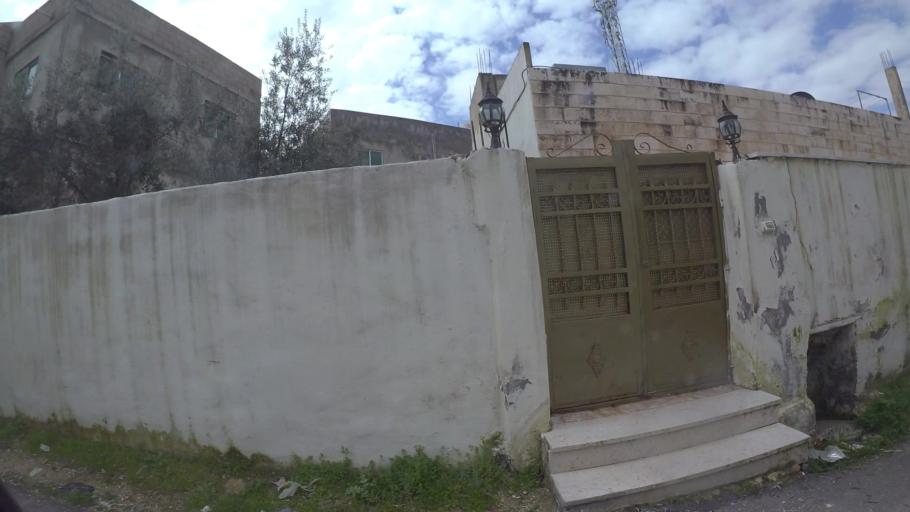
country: JO
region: Amman
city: Al Jubayhah
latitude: 32.0618
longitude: 35.8284
